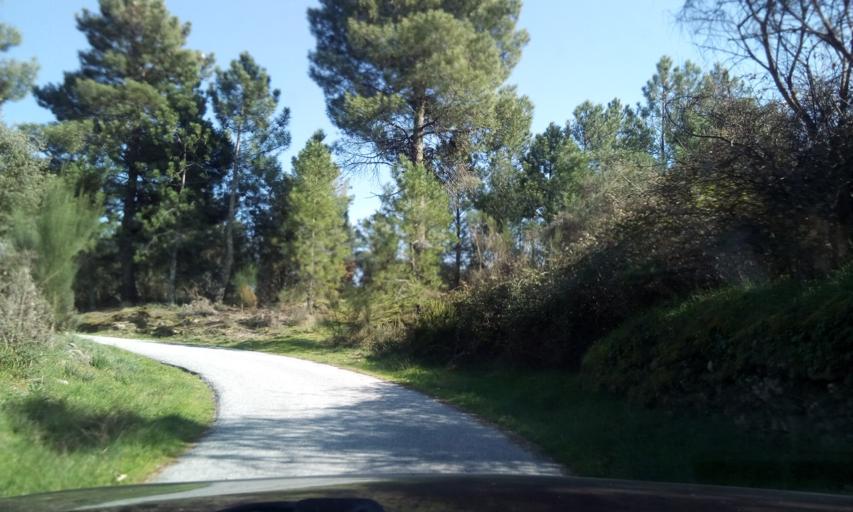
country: PT
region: Guarda
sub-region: Celorico da Beira
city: Celorico da Beira
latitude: 40.6548
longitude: -7.4060
